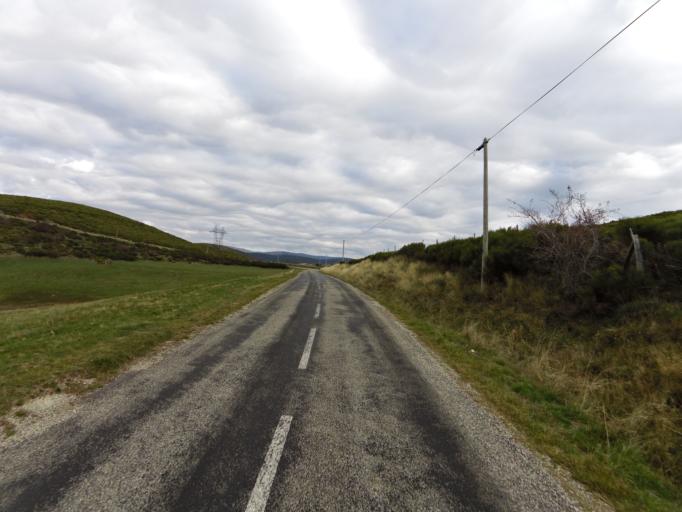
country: FR
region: Rhone-Alpes
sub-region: Departement de l'Ardeche
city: Les Vans
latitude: 44.5452
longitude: 4.0251
